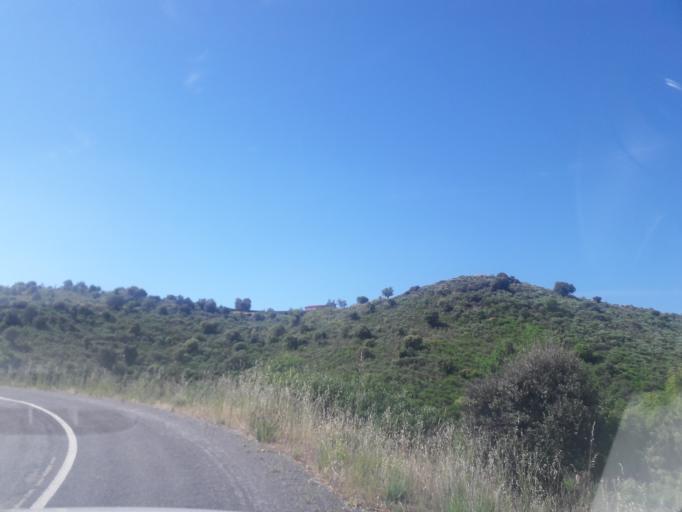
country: ES
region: Castille and Leon
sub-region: Provincia de Salamanca
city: Saucelle
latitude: 41.0135
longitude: -6.7443
